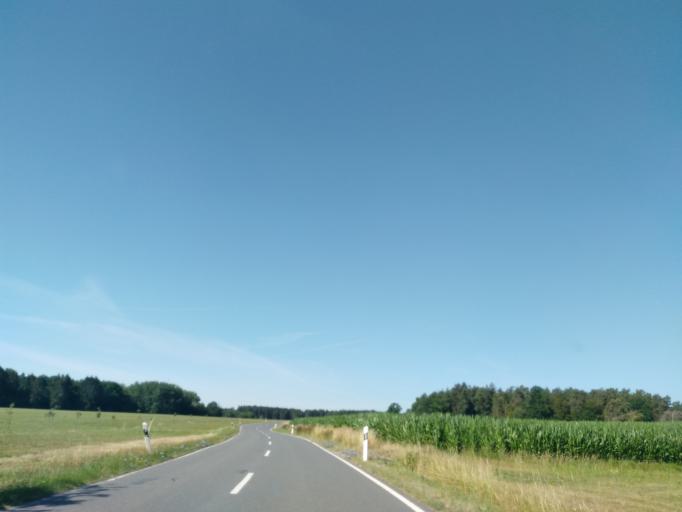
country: DE
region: Baden-Wuerttemberg
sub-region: Karlsruhe Region
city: Mudau
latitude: 49.5476
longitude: 9.2351
